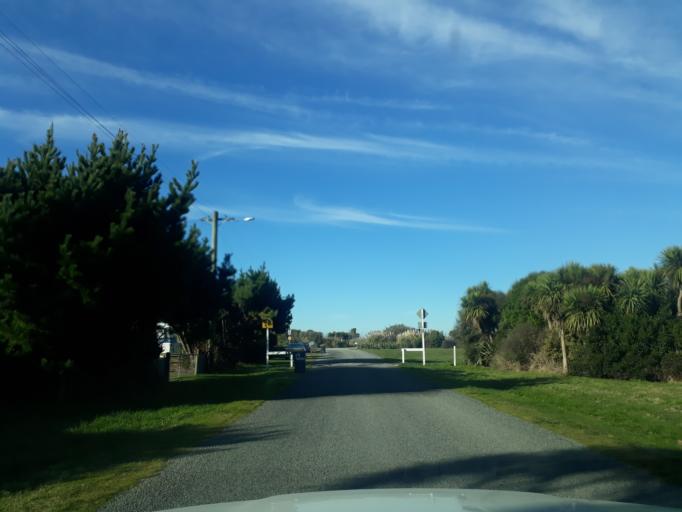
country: NZ
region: Canterbury
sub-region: Timaru District
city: Timaru
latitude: -44.2761
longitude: 171.3500
